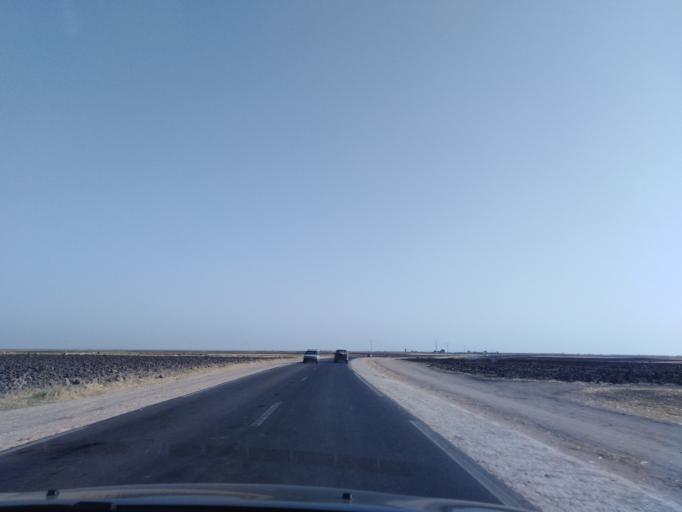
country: MA
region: Doukkala-Abda
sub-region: El-Jadida
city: Sidi Bennour
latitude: 32.5372
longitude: -8.7294
